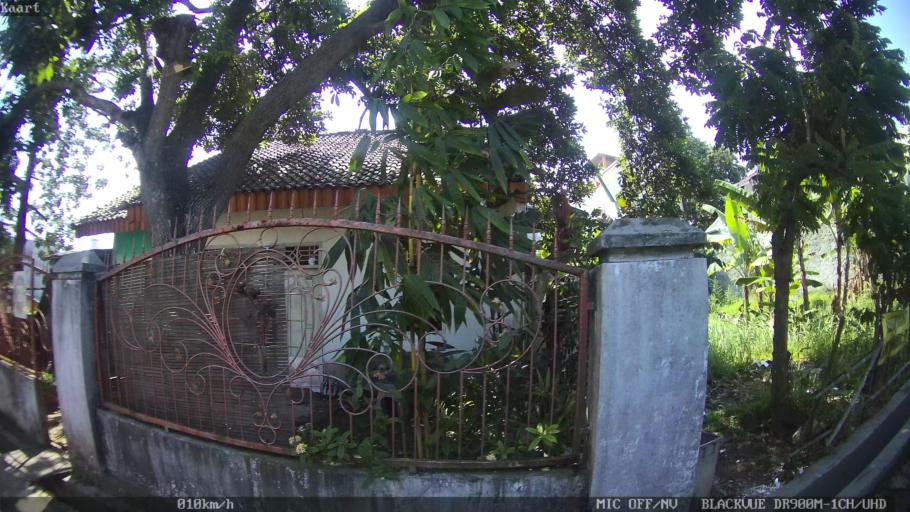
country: ID
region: Lampung
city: Kedaton
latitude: -5.3662
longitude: 105.2546
